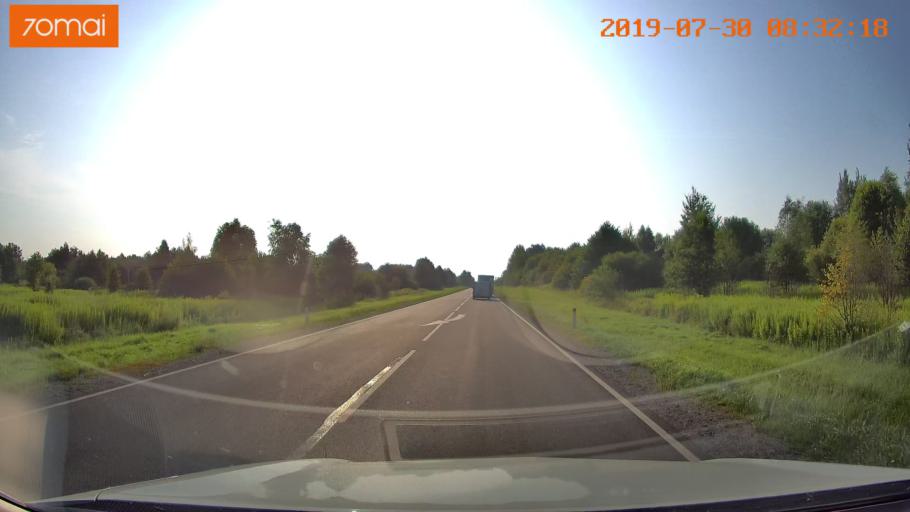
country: RU
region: Kaliningrad
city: Chernyakhovsk
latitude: 54.6381
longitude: 21.7263
